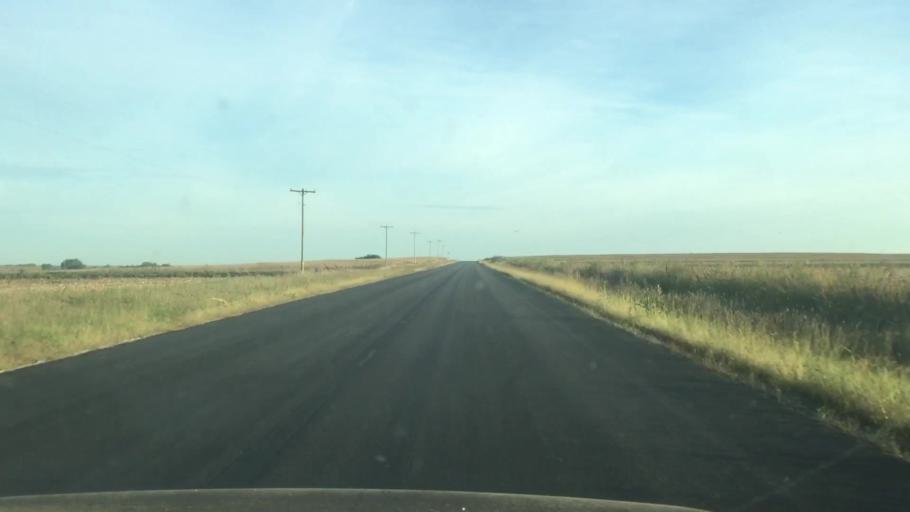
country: US
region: Kansas
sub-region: Marshall County
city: Marysville
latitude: 39.8881
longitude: -96.6010
